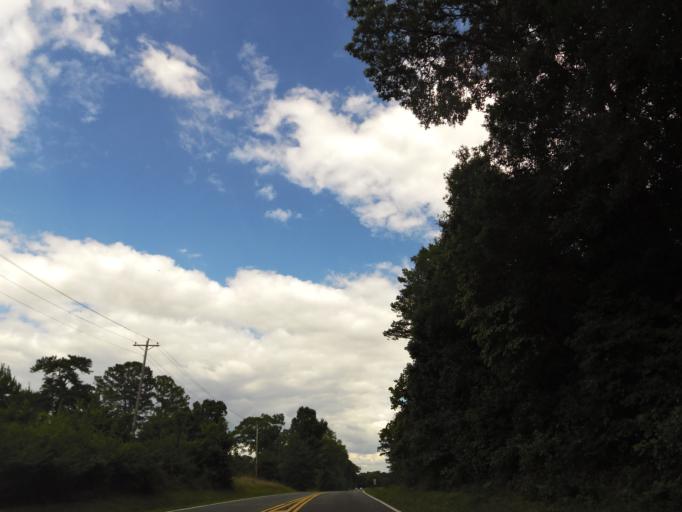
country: US
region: Georgia
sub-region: Catoosa County
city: Fort Oglethorpe
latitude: 34.9415
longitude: -85.2654
